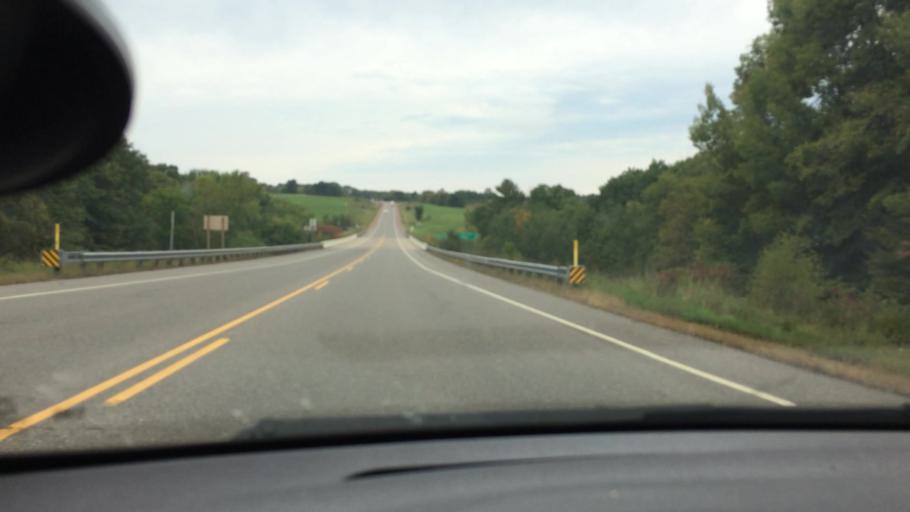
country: US
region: Wisconsin
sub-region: Clark County
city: Neillsville
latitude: 44.5523
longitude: -90.6063
